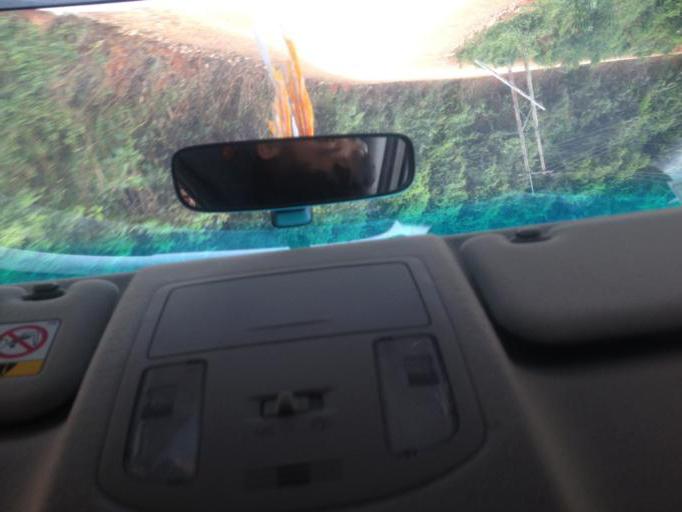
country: TH
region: Nan
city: Chaloem Phra Kiat
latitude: 19.9912
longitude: 101.1401
